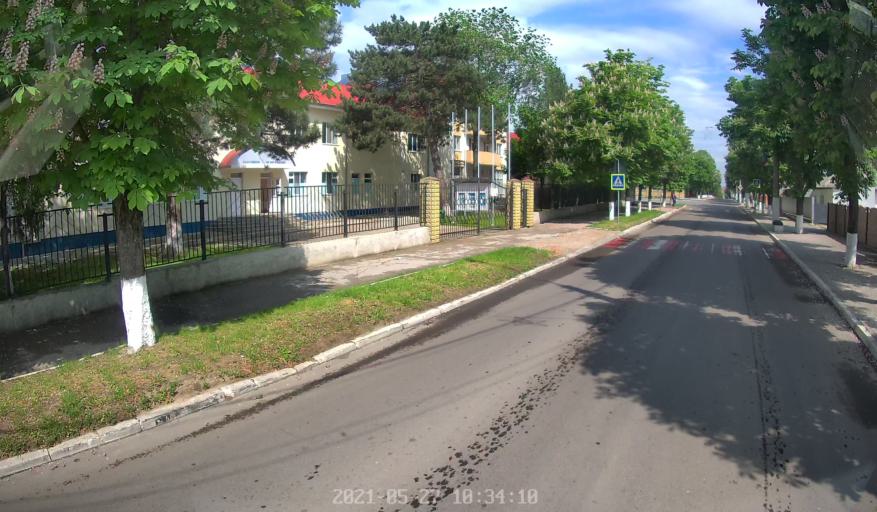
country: MD
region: Chisinau
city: Stauceni
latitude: 47.0889
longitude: 28.8686
